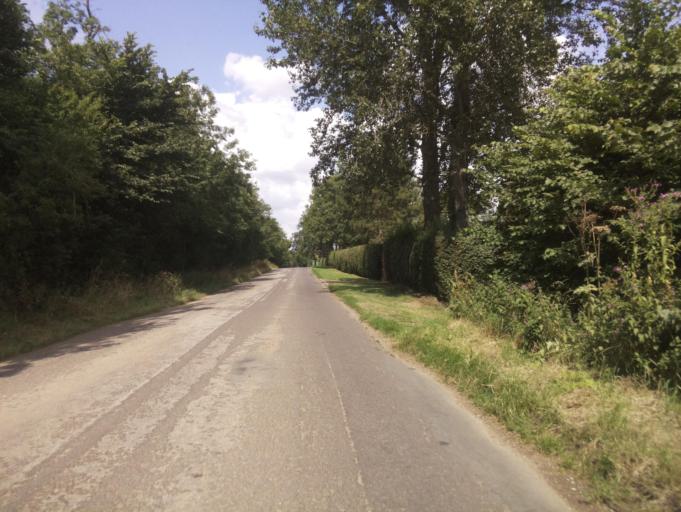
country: GB
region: England
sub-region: Wiltshire
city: Minety
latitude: 51.6089
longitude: -1.9547
